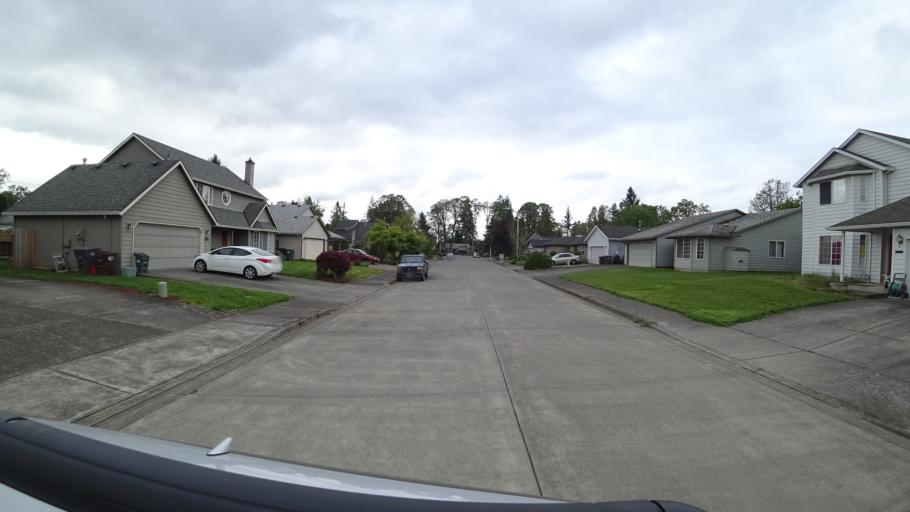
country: US
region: Oregon
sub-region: Washington County
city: Hillsboro
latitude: 45.5319
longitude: -122.9905
